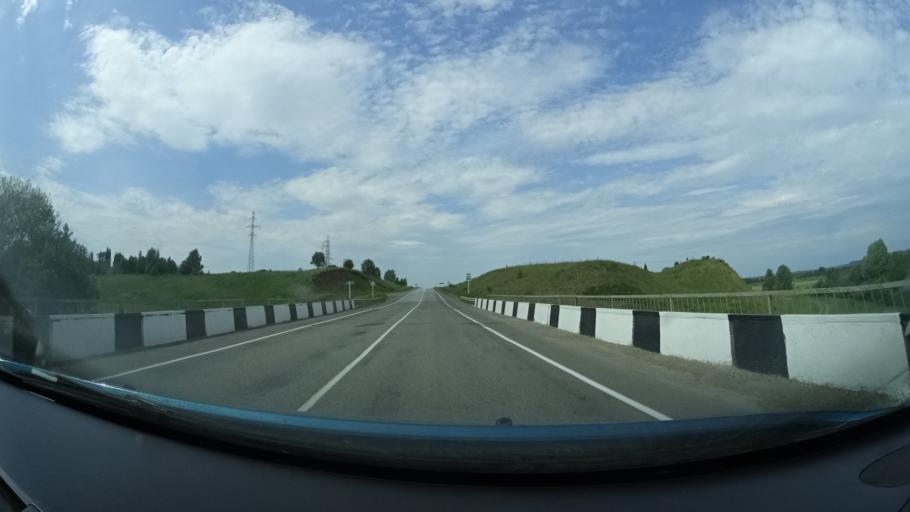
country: RU
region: Perm
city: Barda
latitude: 57.0912
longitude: 55.5366
